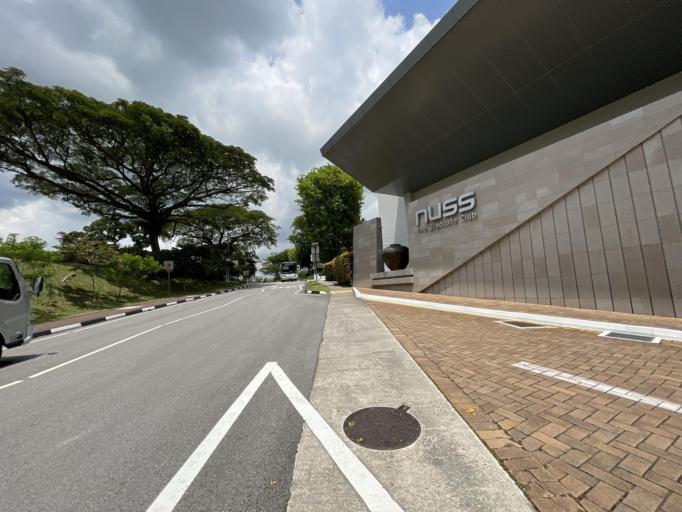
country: SG
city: Singapore
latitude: 1.2932
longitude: 103.7729
